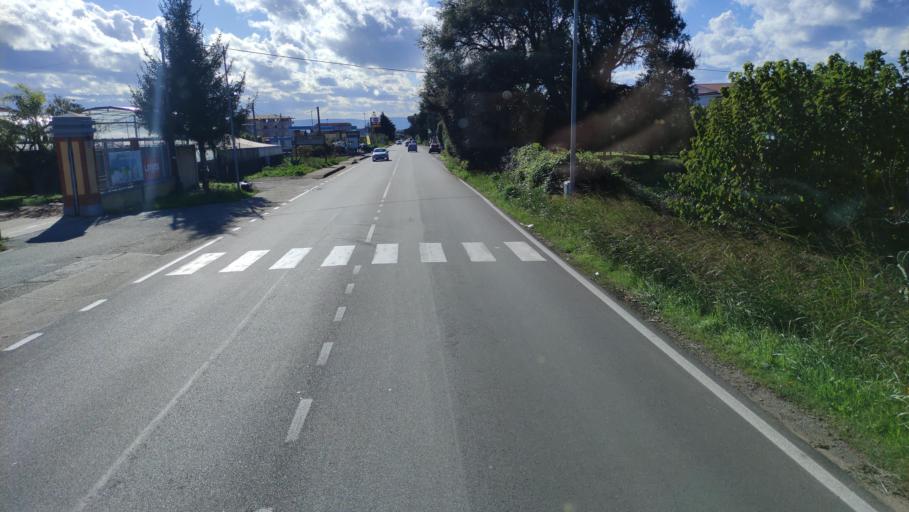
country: IT
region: Calabria
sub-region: Provincia di Catanzaro
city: Nicastro-Sambiase
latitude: 38.9343
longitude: 16.2882
